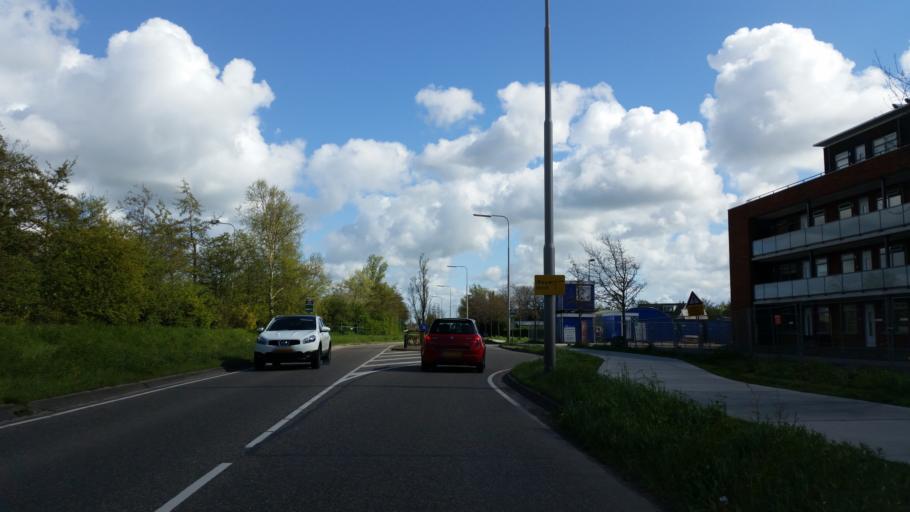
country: NL
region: South Holland
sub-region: Gemeente Teylingen
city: Voorhout
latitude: 52.2303
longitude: 4.4957
